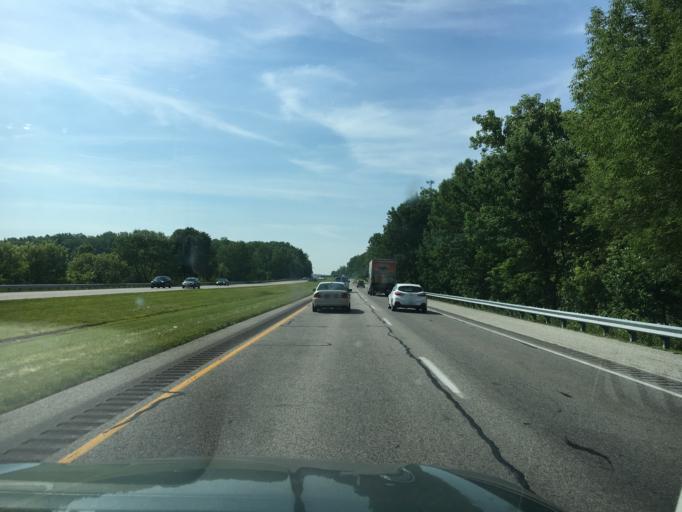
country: US
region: Indiana
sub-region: Decatur County
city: Greensburg
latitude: 39.3929
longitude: -85.5481
